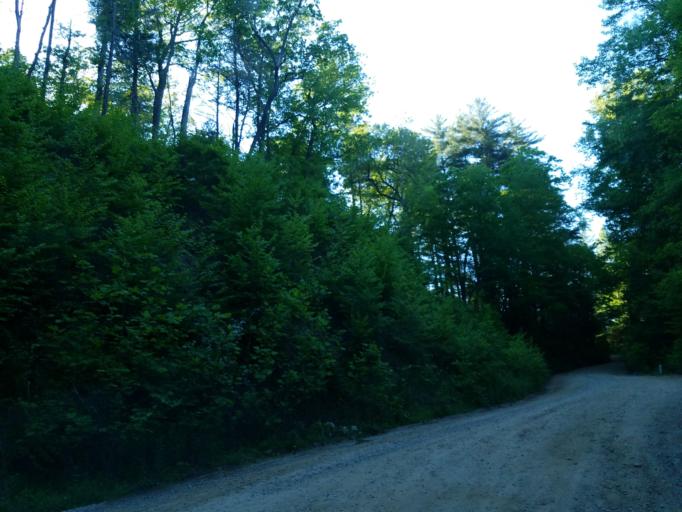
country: US
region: Georgia
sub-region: Fannin County
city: Blue Ridge
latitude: 34.7166
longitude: -84.1517
